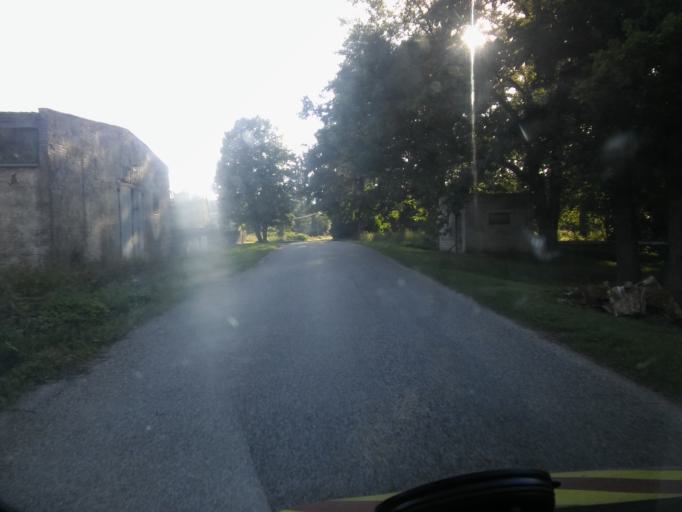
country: EE
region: Valgamaa
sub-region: Torva linn
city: Torva
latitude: 58.0801
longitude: 25.9770
